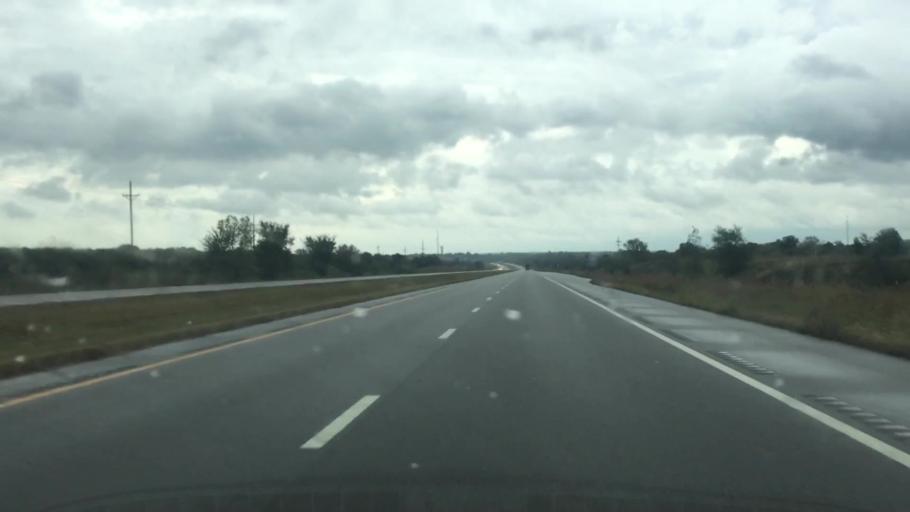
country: US
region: Kansas
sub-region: Miami County
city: Paola
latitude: 38.5382
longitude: -94.8857
